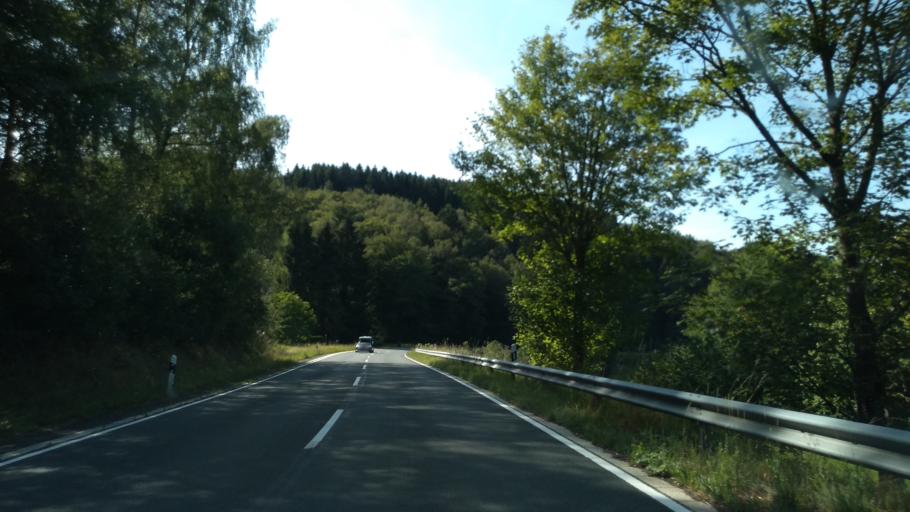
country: DE
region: North Rhine-Westphalia
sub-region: Regierungsbezirk Arnsberg
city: Olpe
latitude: 51.0545
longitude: 7.8567
